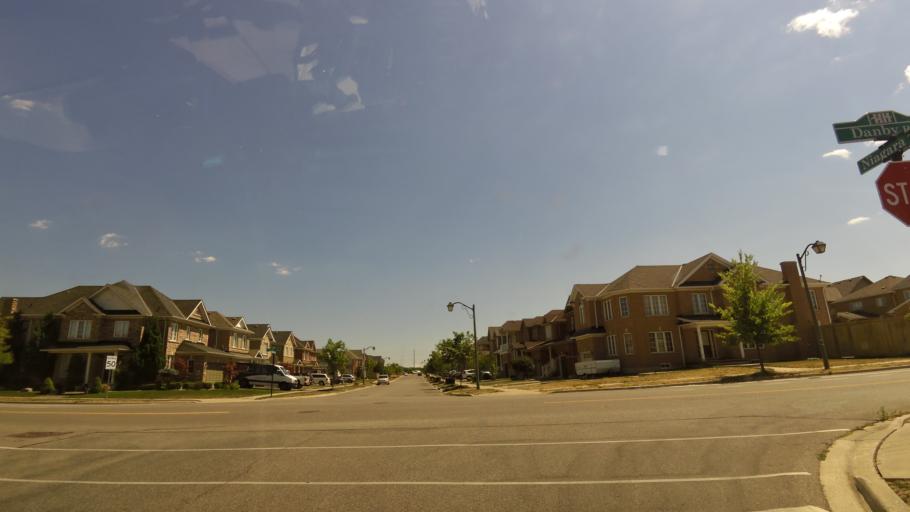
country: CA
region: Ontario
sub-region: Halton
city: Milton
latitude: 43.6311
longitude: -79.8742
